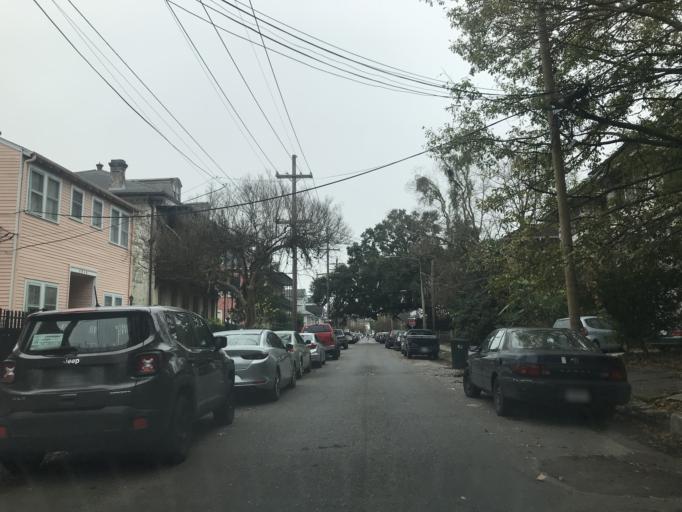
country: US
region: Louisiana
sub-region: Orleans Parish
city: New Orleans
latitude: 29.9331
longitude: -90.0766
